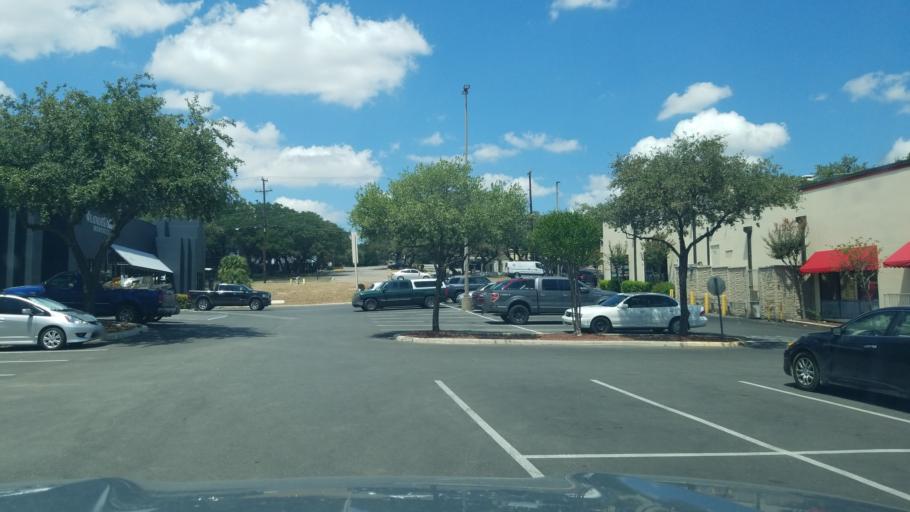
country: US
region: Texas
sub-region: Bexar County
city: Hollywood Park
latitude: 29.5647
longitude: -98.4893
